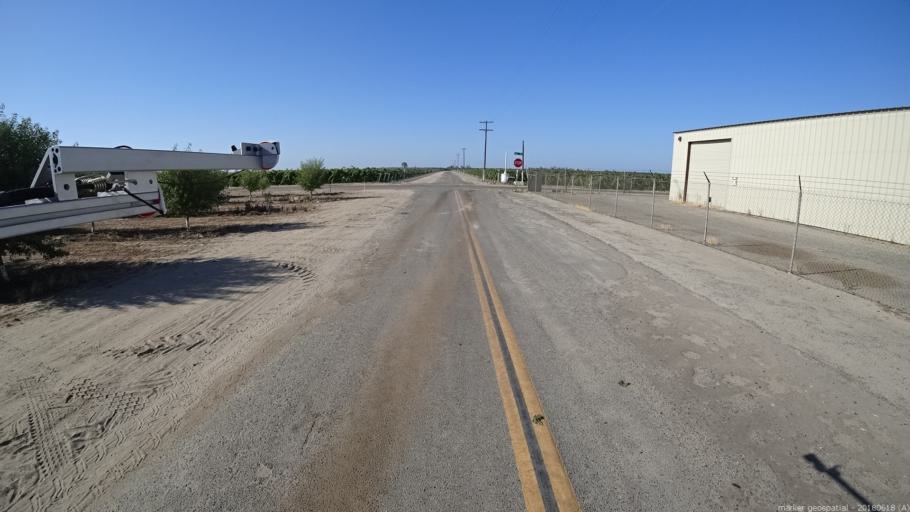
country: US
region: California
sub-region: Fresno County
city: Biola
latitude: 36.8299
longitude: -120.1059
